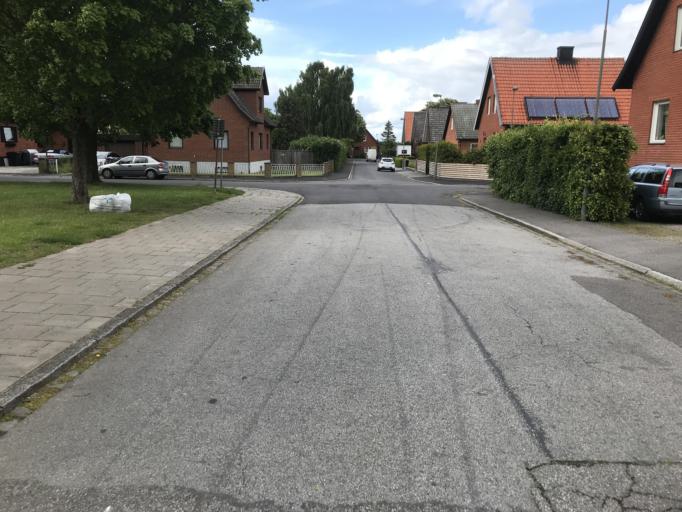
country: SE
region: Skane
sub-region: Burlovs Kommun
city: Arloev
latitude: 55.5846
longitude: 13.0635
